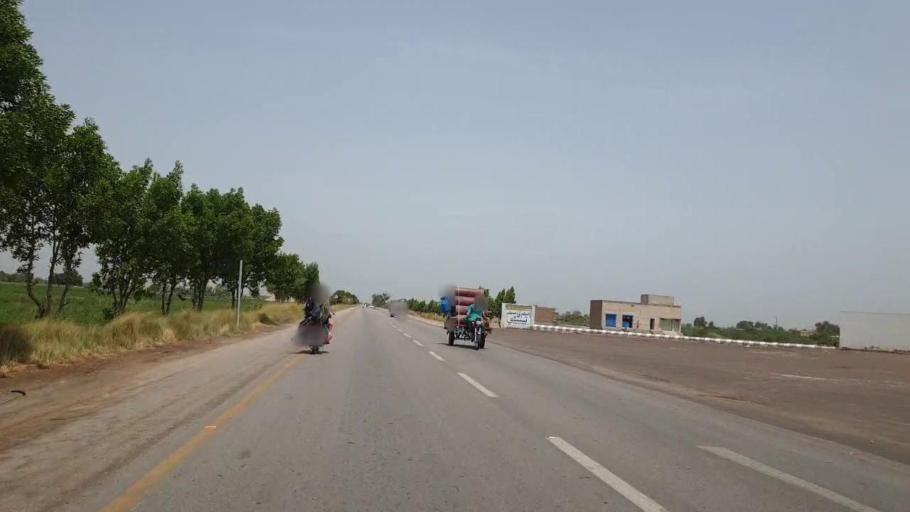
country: PK
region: Sindh
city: Nawabshah
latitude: 26.2238
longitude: 68.4953
